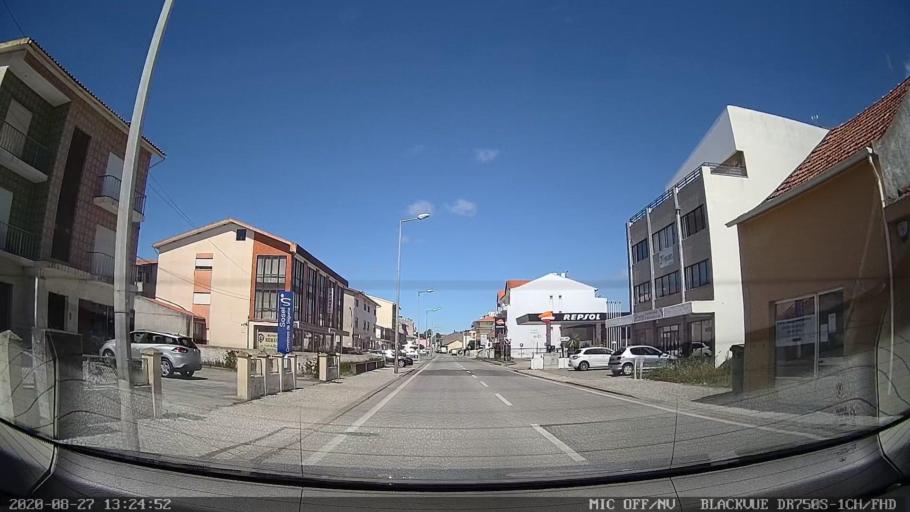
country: PT
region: Aveiro
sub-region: Vagos
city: Vagos
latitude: 40.5506
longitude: -8.6799
